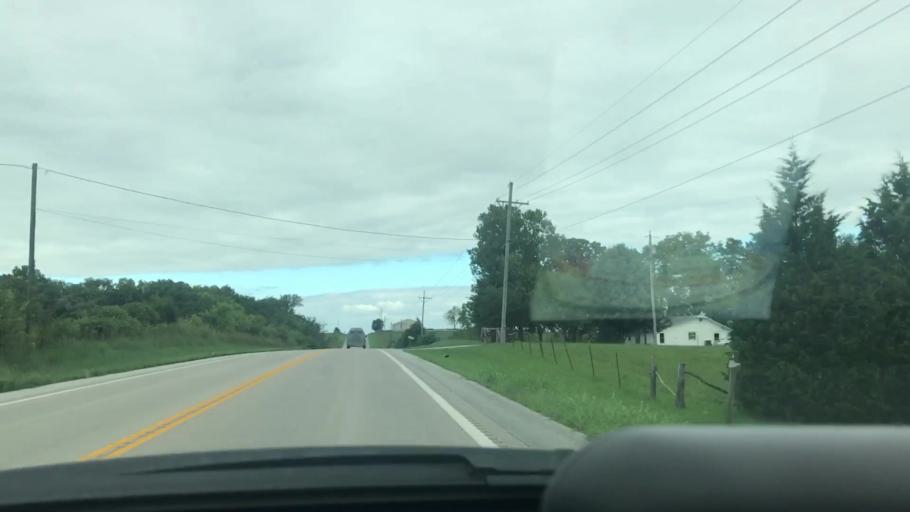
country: US
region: Missouri
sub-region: Hickory County
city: Hermitage
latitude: 37.8796
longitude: -93.1803
